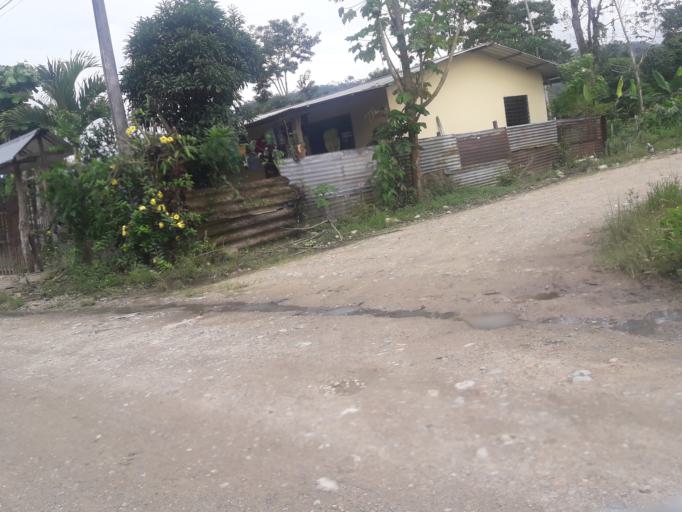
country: EC
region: Napo
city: Tena
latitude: -0.9794
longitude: -77.8467
